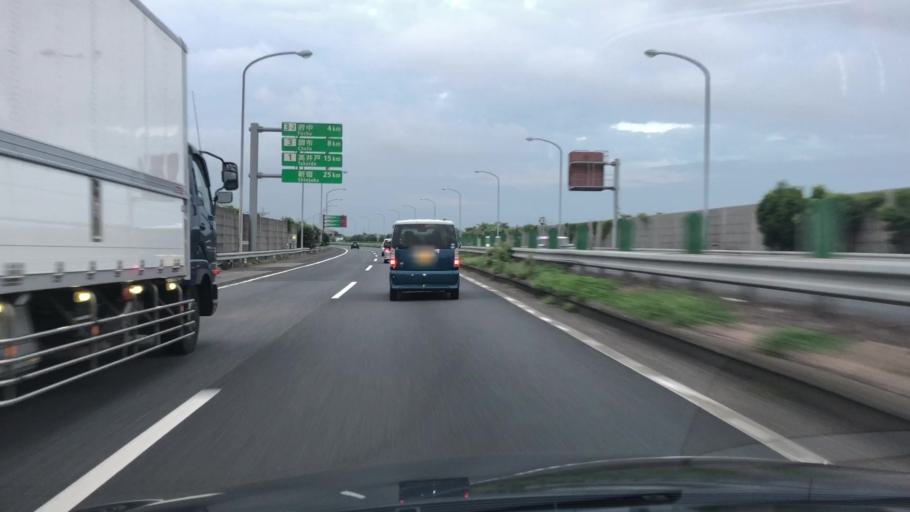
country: JP
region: Tokyo
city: Kokubunji
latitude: 35.6671
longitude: 139.4484
